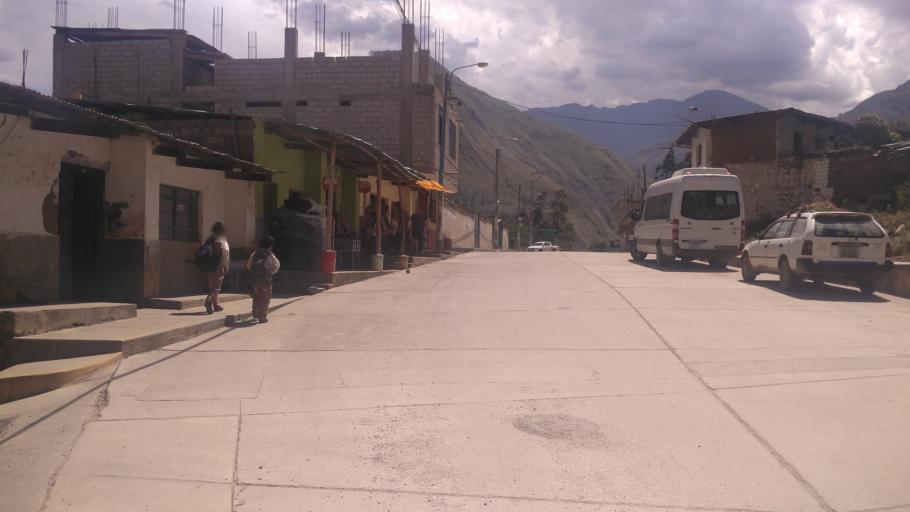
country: PE
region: Cusco
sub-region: Provincia de La Convencion
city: Santa Teresa
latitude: -13.1316
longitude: -72.5952
